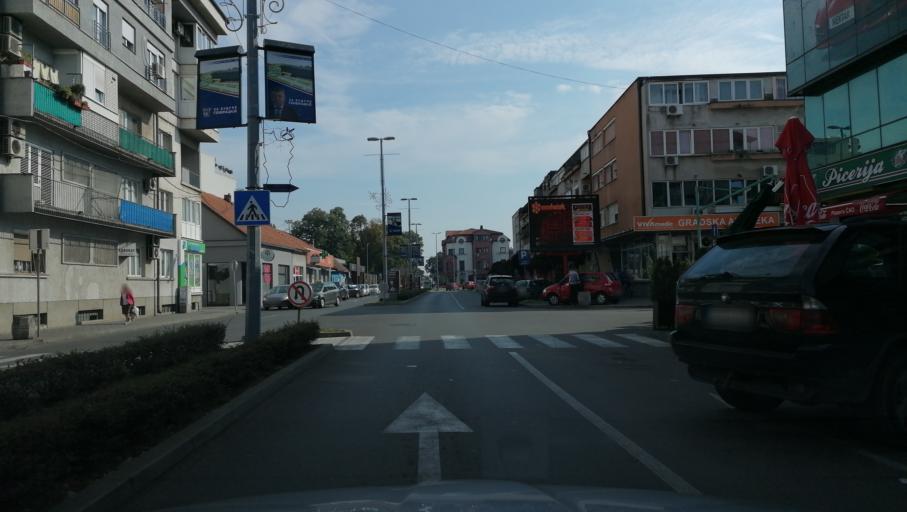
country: BA
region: Republika Srpska
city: Bijeljina
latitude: 44.7553
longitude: 19.2165
